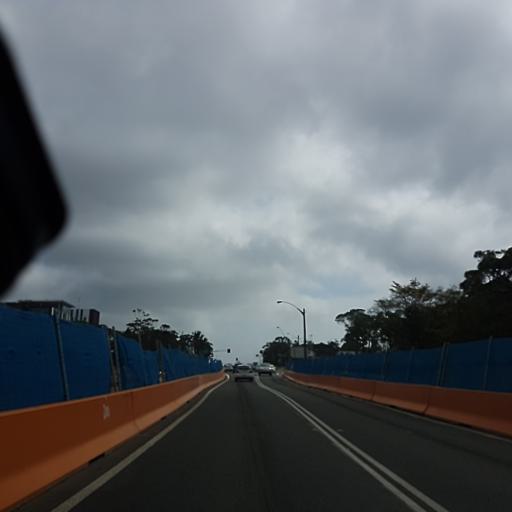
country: AU
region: New South Wales
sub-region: Warringah
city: Allambie Heights
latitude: -33.7542
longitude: 151.2340
